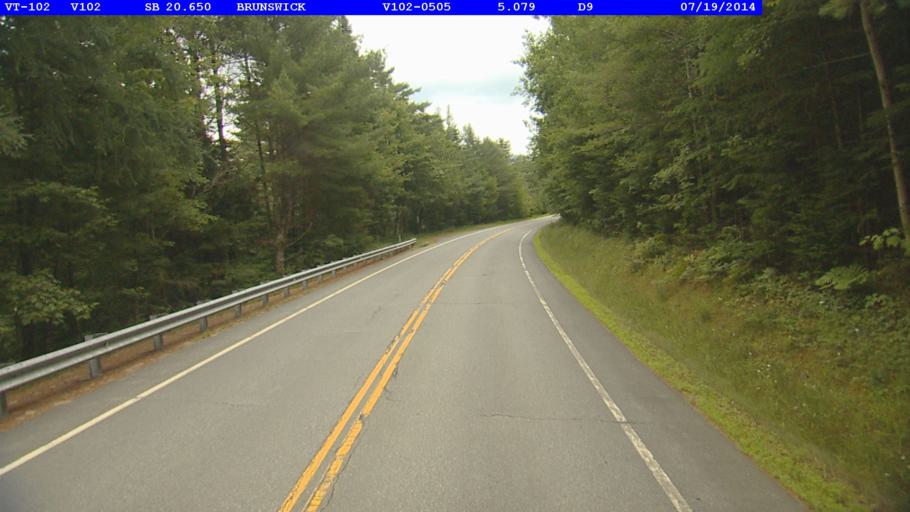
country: US
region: New Hampshire
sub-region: Coos County
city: Stratford
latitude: 44.7242
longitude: -71.6282
